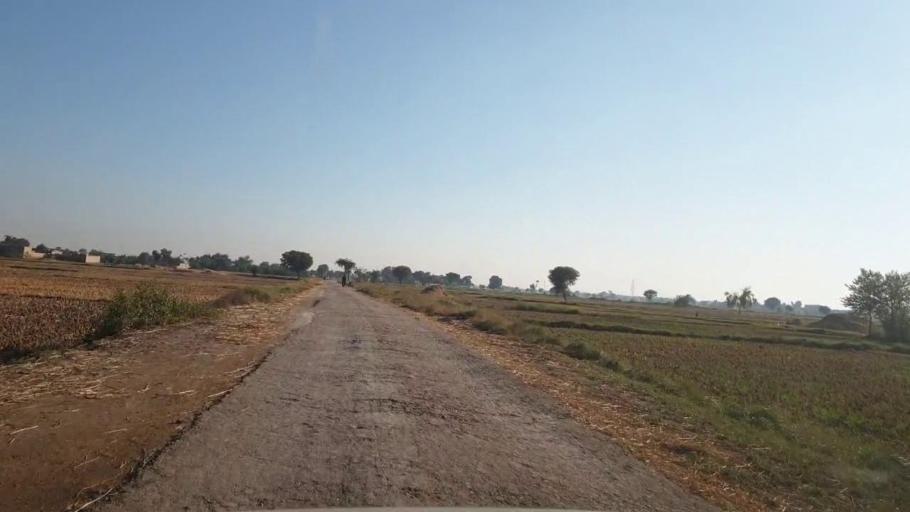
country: PK
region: Sindh
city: Phulji
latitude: 26.9862
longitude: 67.6905
